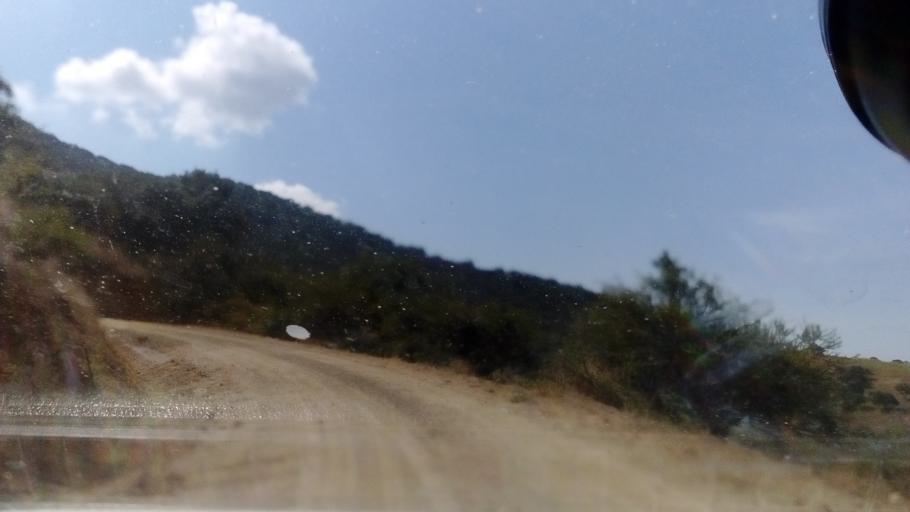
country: MX
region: Guanajuato
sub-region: Silao de la Victoria
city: San Francisco (Banos de Agua Caliente)
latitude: 21.1725
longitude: -101.4585
